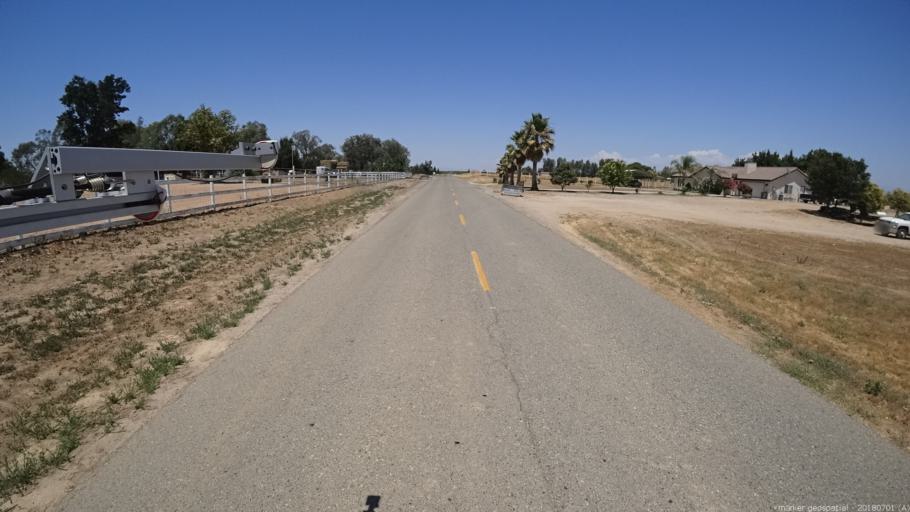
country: US
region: California
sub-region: Madera County
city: Madera Acres
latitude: 37.0625
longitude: -120.0246
